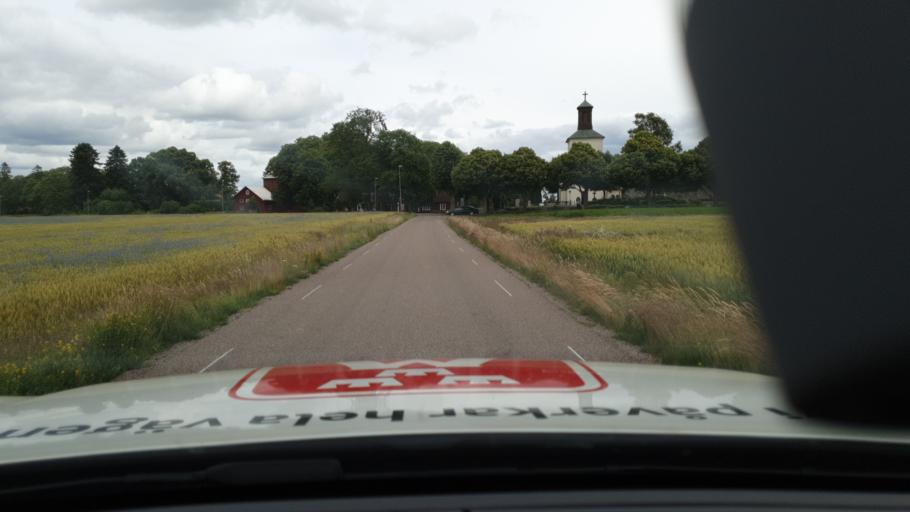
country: SE
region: Vaestra Goetaland
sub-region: Skara Kommun
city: Skara
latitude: 58.3999
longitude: 13.3758
